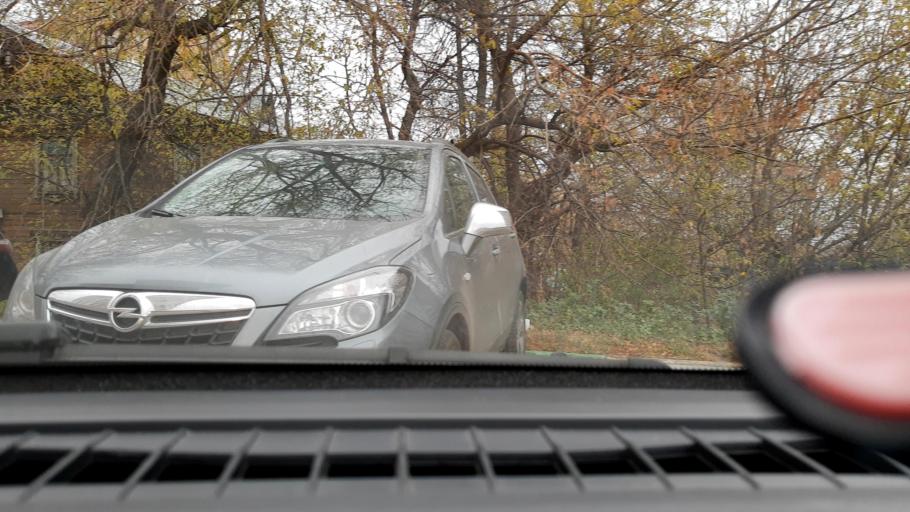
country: RU
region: Nizjnij Novgorod
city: Nizhniy Novgorod
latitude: 56.3041
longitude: 43.9978
